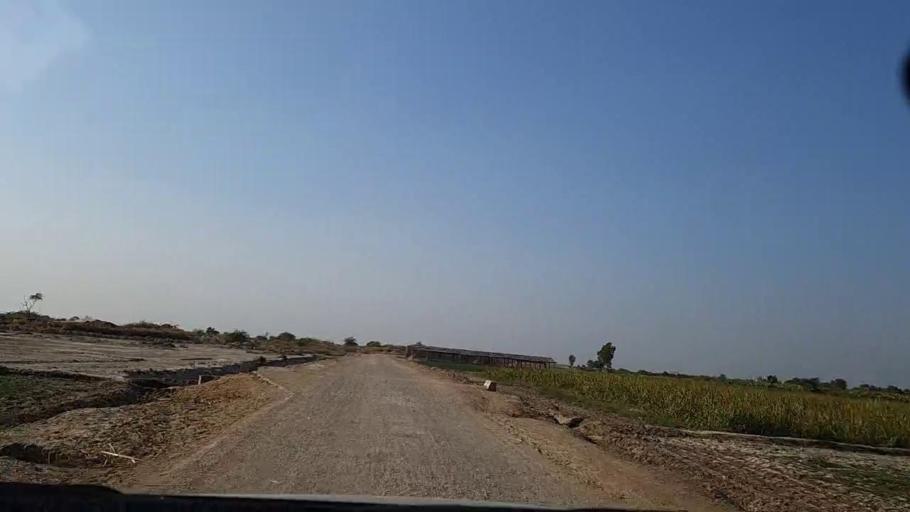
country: PK
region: Sindh
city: Mirwah Gorchani
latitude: 25.2295
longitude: 68.9829
